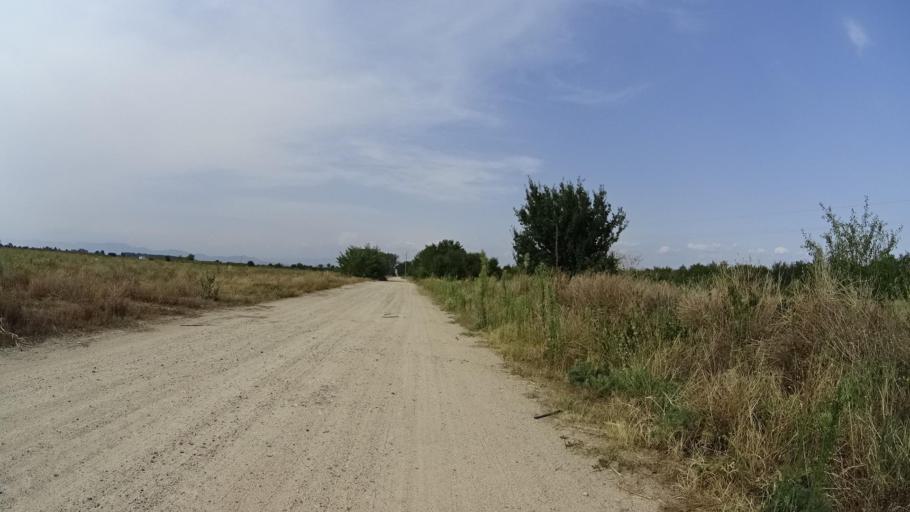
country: BG
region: Plovdiv
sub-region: Obshtina Kaloyanovo
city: Kaloyanovo
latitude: 42.3015
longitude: 24.7990
